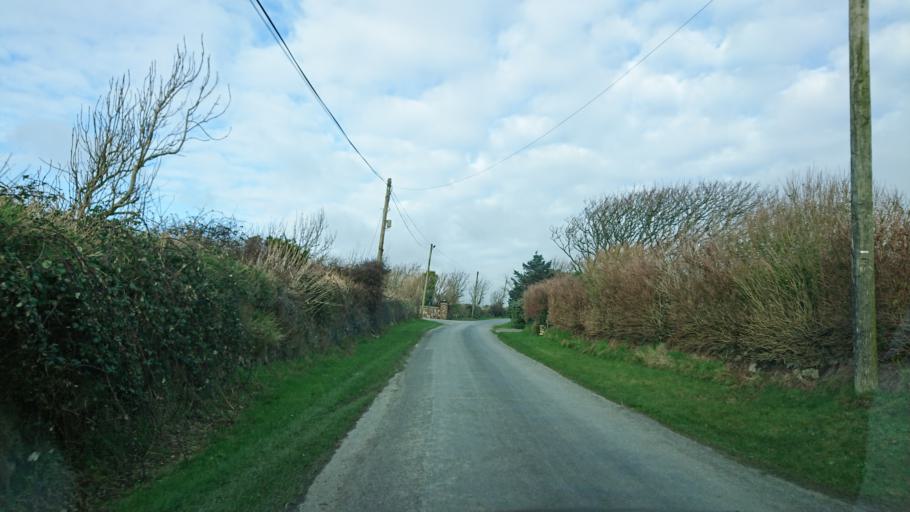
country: IE
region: Munster
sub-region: Waterford
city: Portlaw
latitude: 52.1400
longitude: -7.3058
